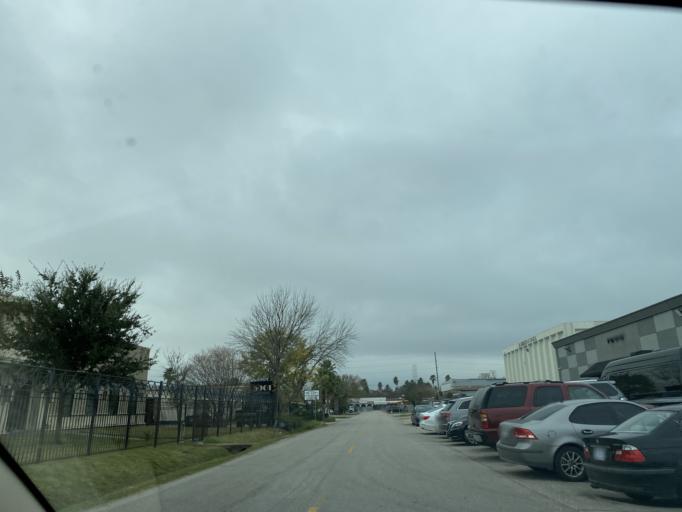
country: US
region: Texas
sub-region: Harris County
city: Bellaire
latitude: 29.7288
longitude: -95.4817
